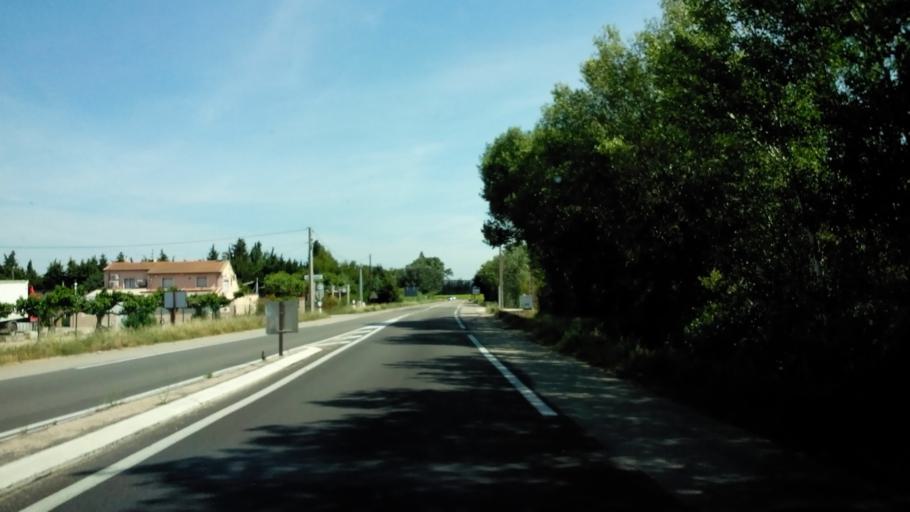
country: FR
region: Languedoc-Roussillon
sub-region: Departement du Gard
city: Les Angles
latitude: 43.9775
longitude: 4.7481
